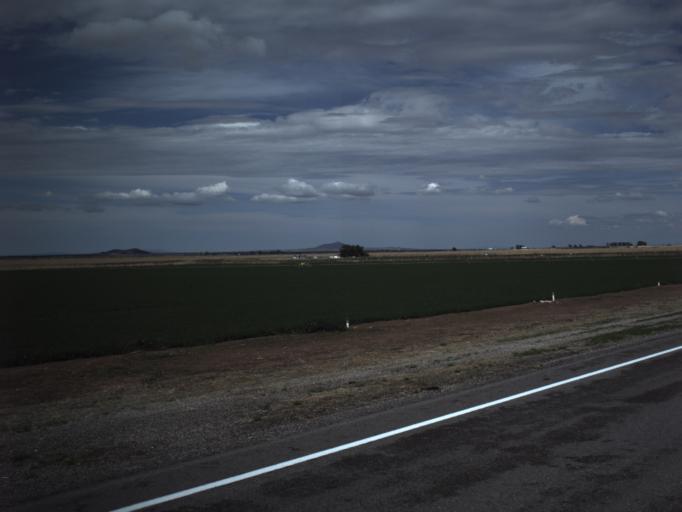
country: US
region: Utah
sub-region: Millard County
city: Fillmore
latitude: 38.8626
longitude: -112.4181
